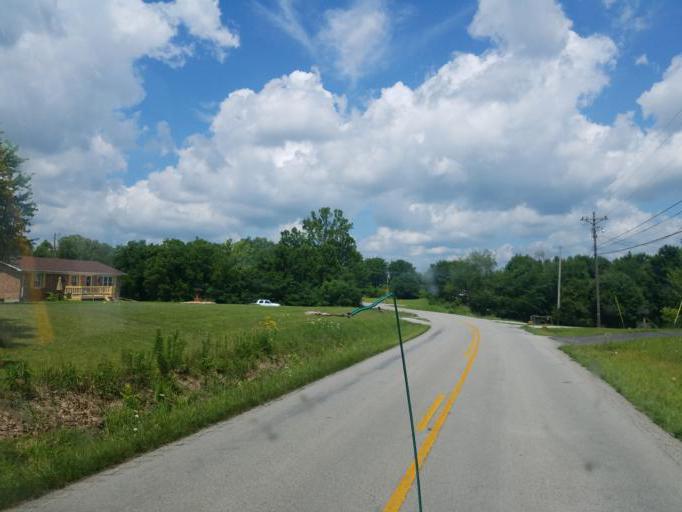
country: US
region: Kentucky
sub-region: Grayson County
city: Leitchfield
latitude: 37.5062
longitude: -86.3169
